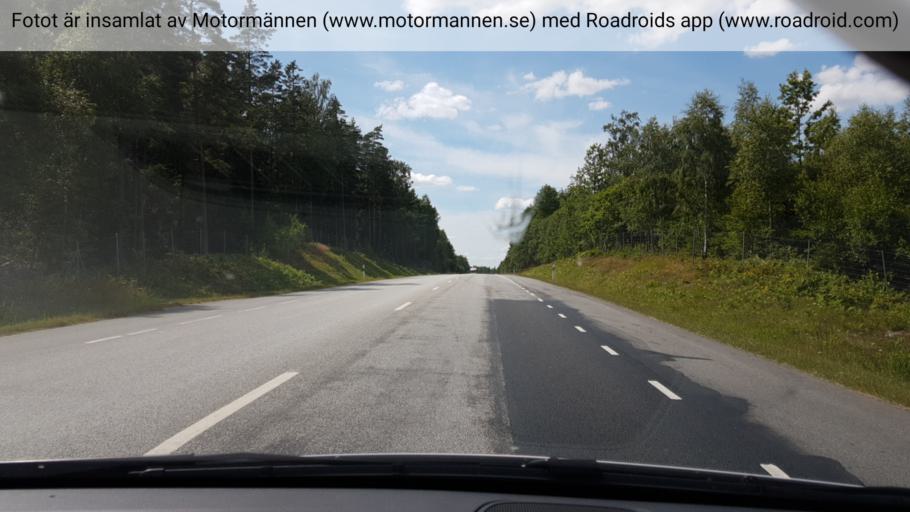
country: SE
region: Vaestra Goetaland
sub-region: Mariestads Kommun
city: Mariestad
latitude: 58.6694
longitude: 13.7921
